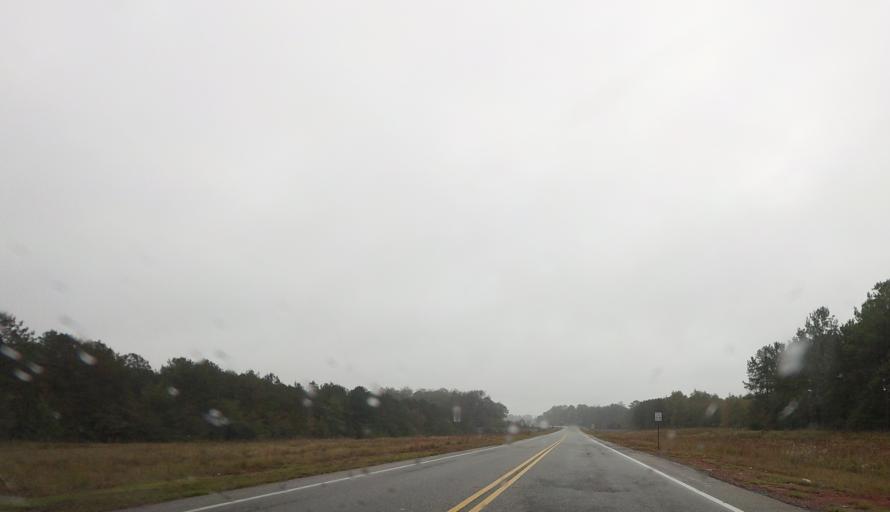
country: US
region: Georgia
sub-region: Peach County
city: Fort Valley
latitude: 32.5387
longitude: -83.9075
